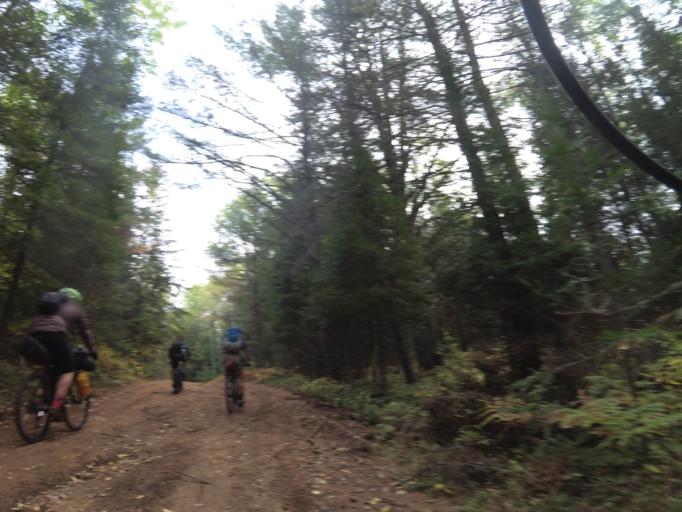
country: CA
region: Ontario
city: Pembroke
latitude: 45.2719
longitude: -77.2316
